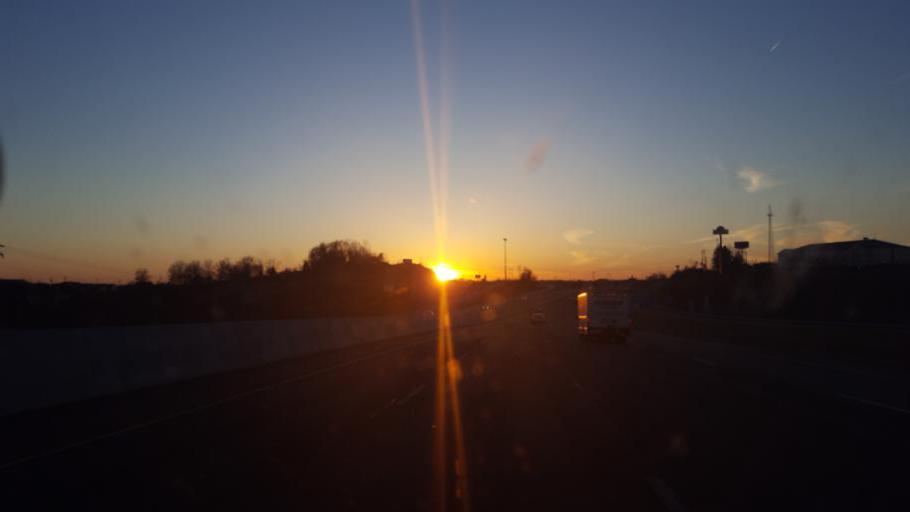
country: US
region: Ohio
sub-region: Belmont County
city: Saint Clairsville
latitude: 40.0698
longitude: -80.8536
